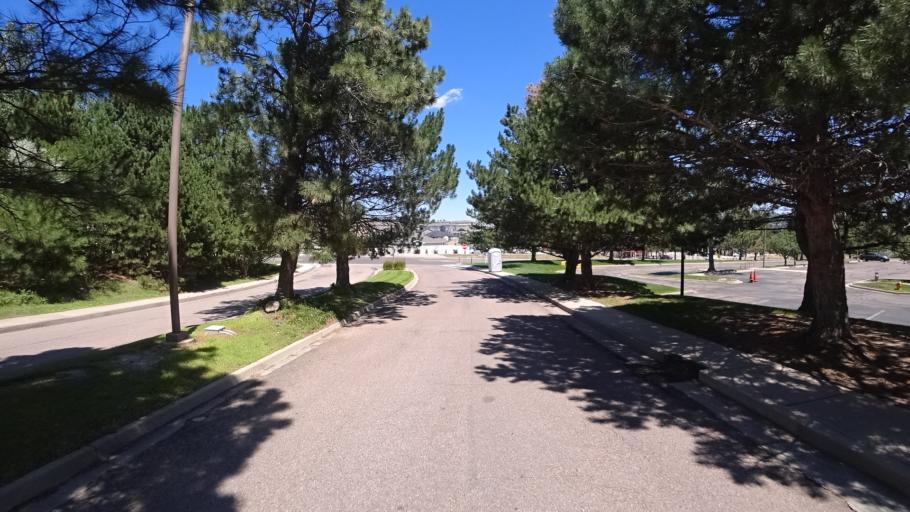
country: US
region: Colorado
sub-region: El Paso County
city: Colorado Springs
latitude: 38.9140
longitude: -104.8274
